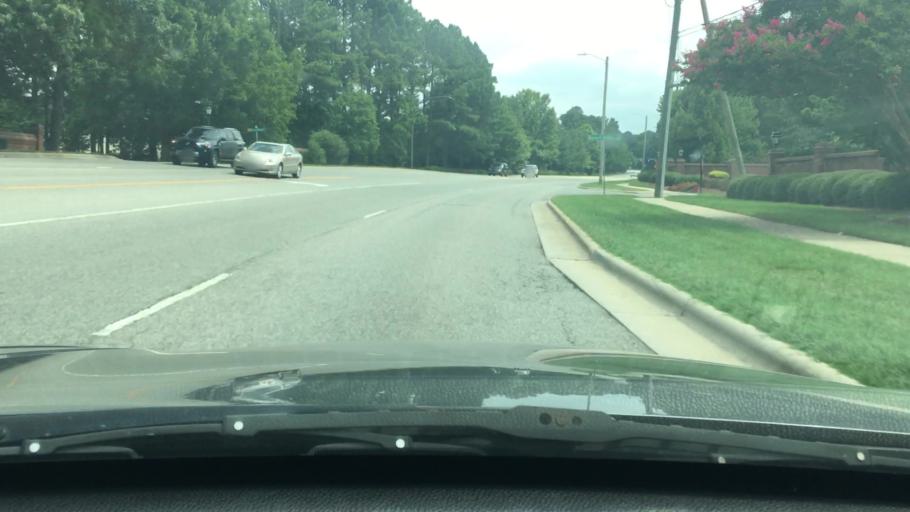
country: US
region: North Carolina
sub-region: Wake County
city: West Raleigh
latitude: 35.8313
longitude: -78.7106
